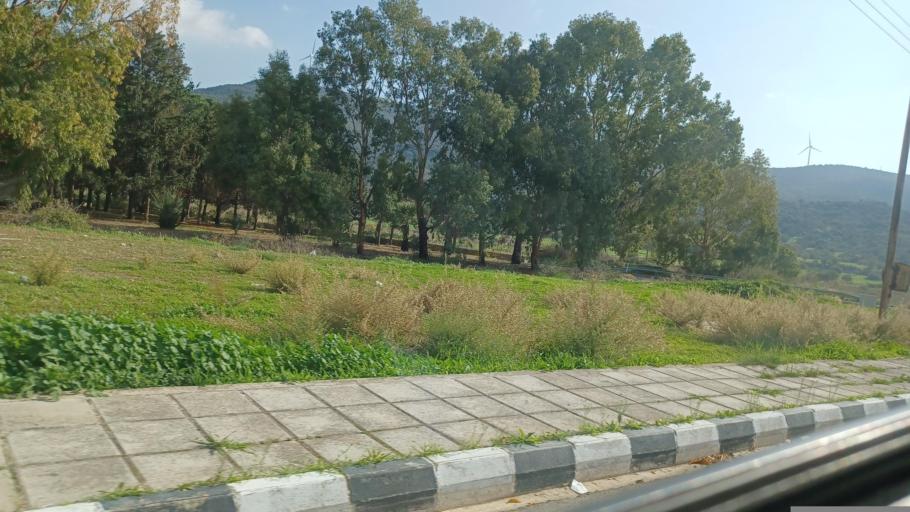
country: CY
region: Limassol
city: Pissouri
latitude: 34.7605
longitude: 32.6242
